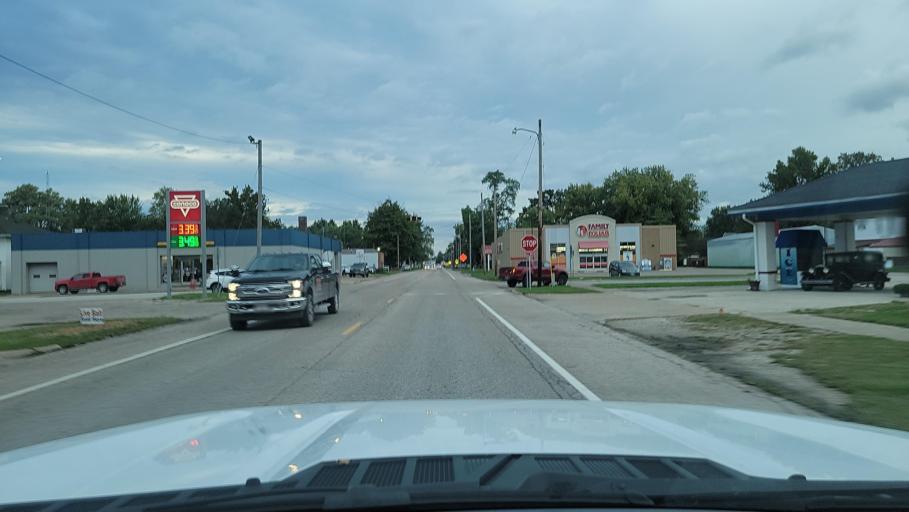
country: US
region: Illinois
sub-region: Schuyler County
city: Rushville
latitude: 40.1234
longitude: -90.5636
